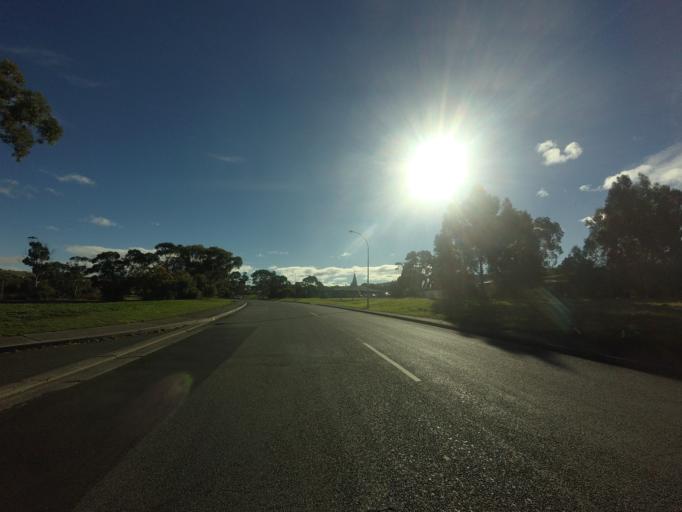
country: AU
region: Tasmania
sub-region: Clarence
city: Rokeby
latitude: -42.8957
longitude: 147.4463
